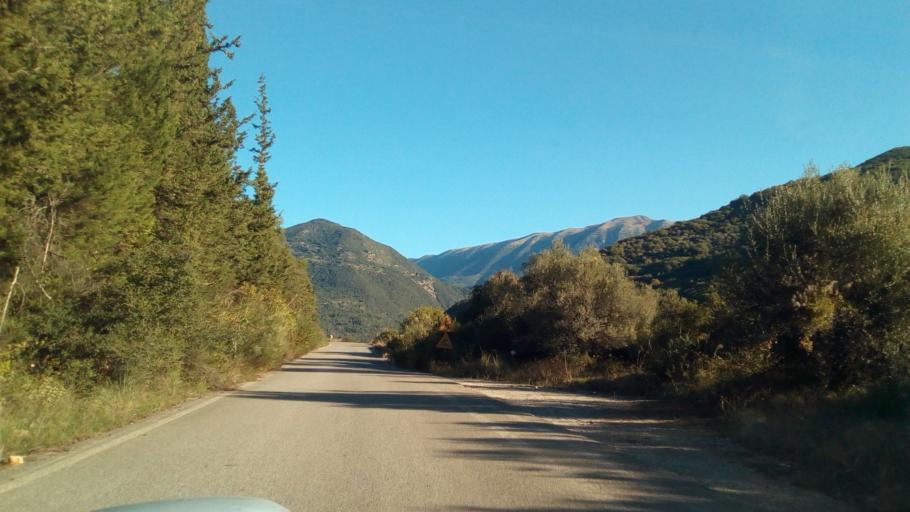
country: GR
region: West Greece
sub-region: Nomos Aitolias kai Akarnanias
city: Nafpaktos
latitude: 38.4443
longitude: 21.8841
